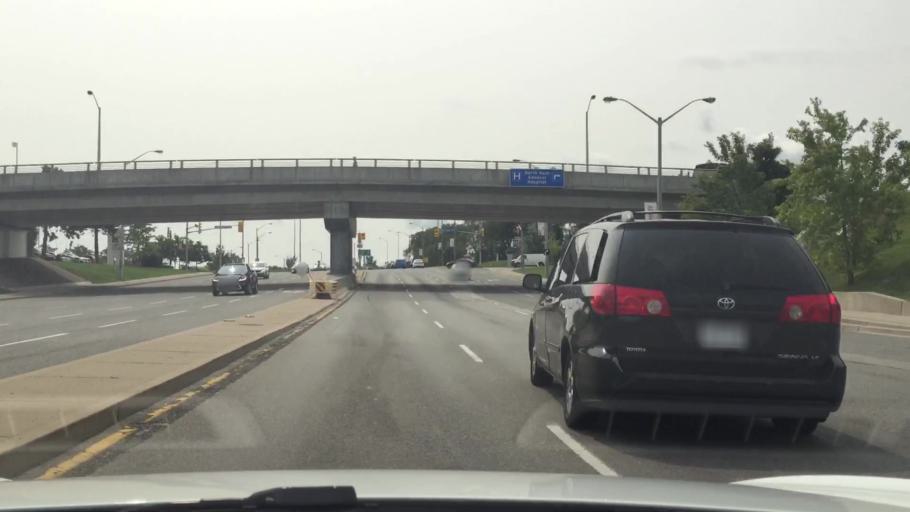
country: CA
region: Ontario
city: Willowdale
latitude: 43.7706
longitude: -79.3643
